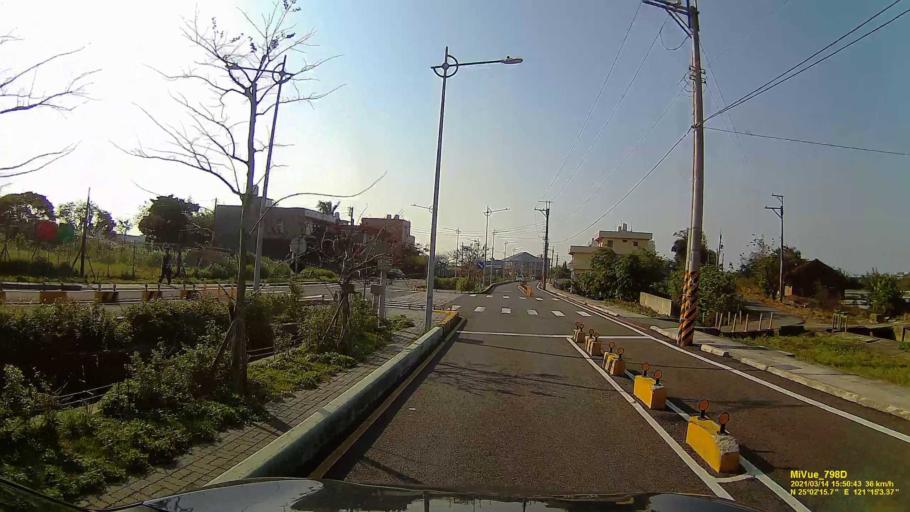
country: TW
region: Taiwan
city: Taoyuan City
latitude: 25.0378
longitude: 121.2508
